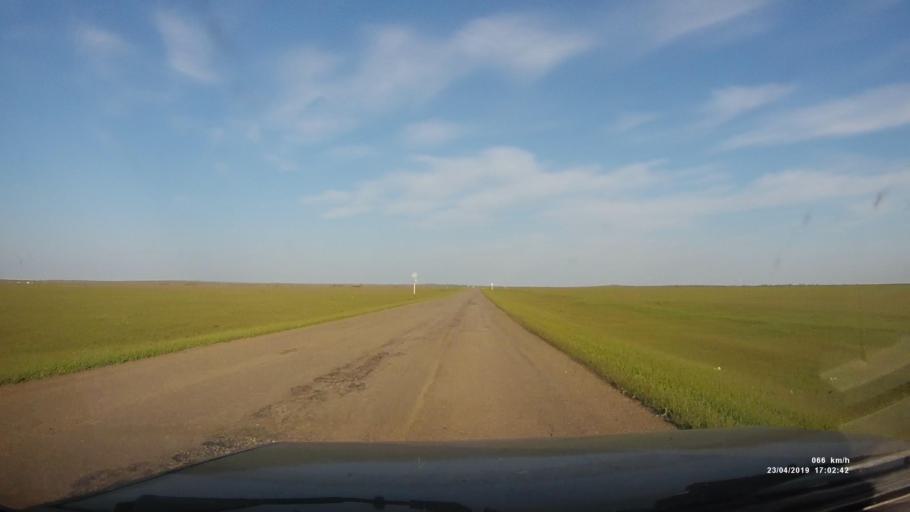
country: RU
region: Kalmykiya
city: Priyutnoye
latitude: 46.2919
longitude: 43.4211
